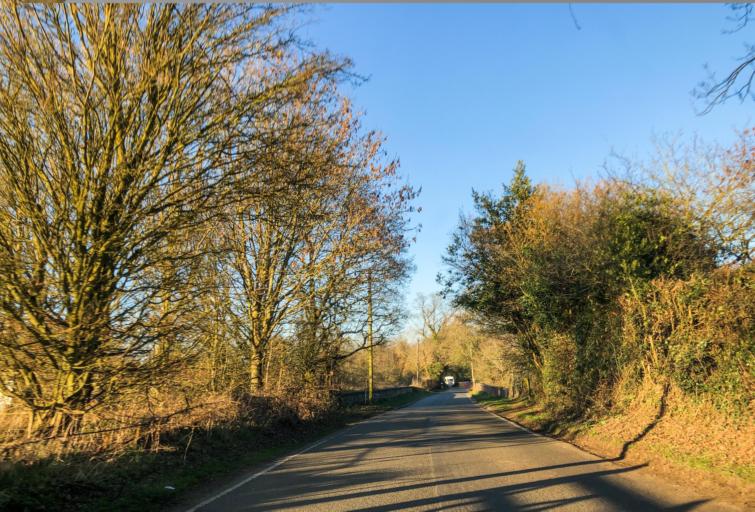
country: GB
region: England
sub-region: Warwickshire
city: Wroxall
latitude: 52.2966
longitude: -1.6585
